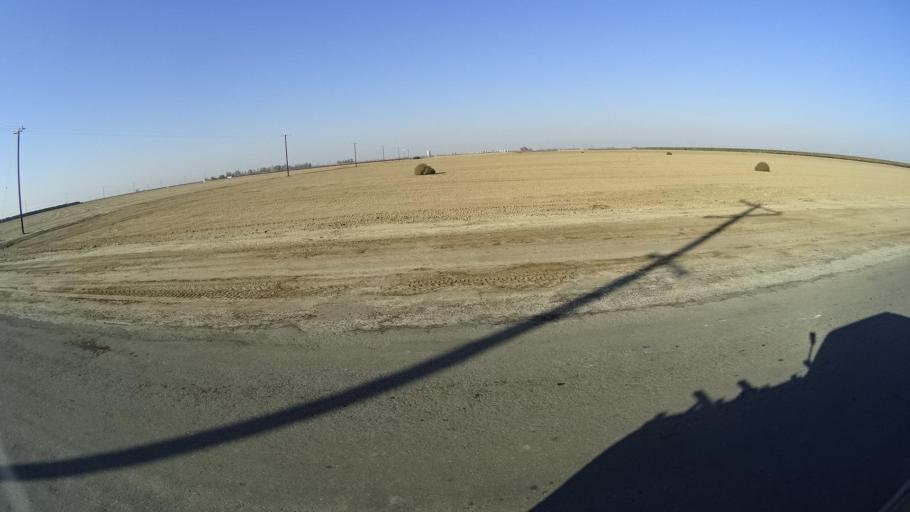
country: US
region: California
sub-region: Tulare County
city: Richgrove
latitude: 35.7799
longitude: -119.1608
